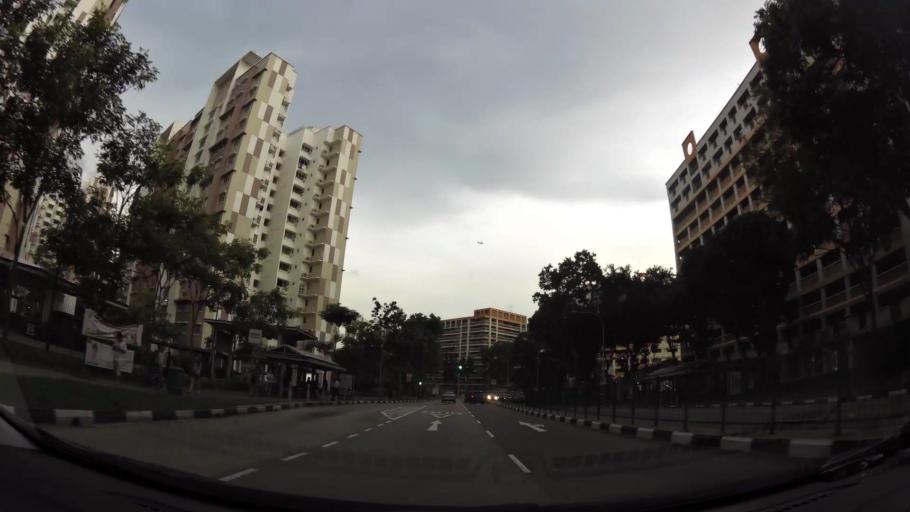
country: MY
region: Johor
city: Kampung Pasir Gudang Baru
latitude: 1.4321
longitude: 103.8418
